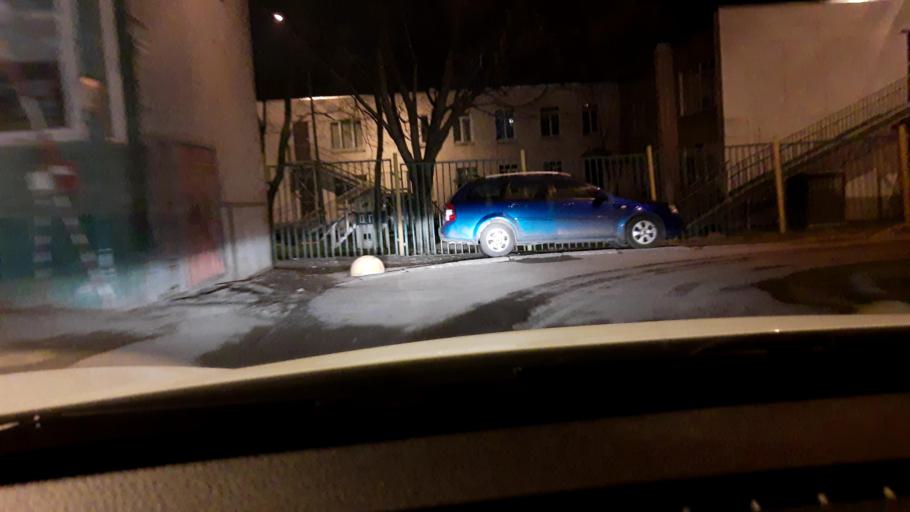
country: RU
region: Moscow
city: Yasenevo
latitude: 55.5975
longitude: 37.5436
